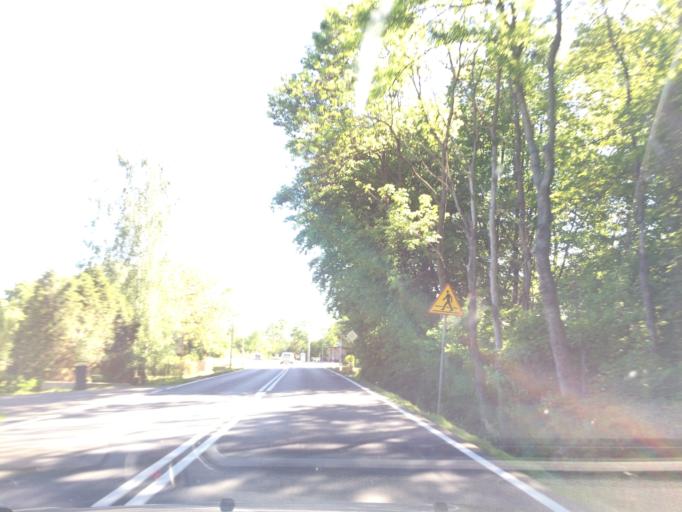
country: PL
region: Lower Silesian Voivodeship
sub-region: Powiat wroclawski
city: Sobotka
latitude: 50.9258
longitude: 16.6830
